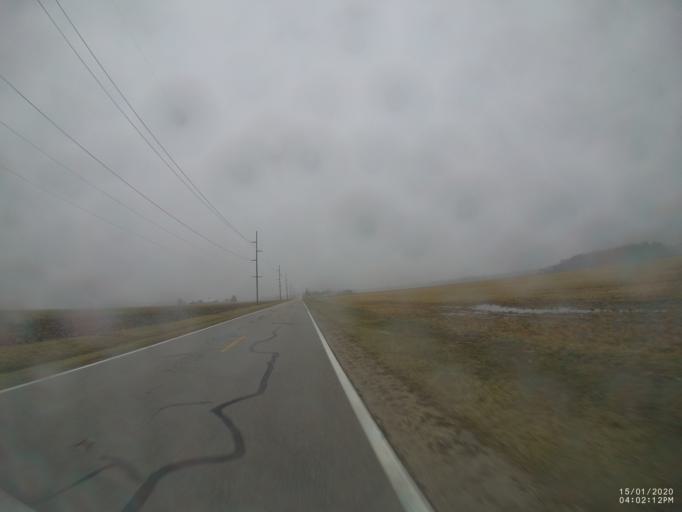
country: US
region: Ohio
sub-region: Sandusky County
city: Woodville
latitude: 41.4136
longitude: -83.3690
